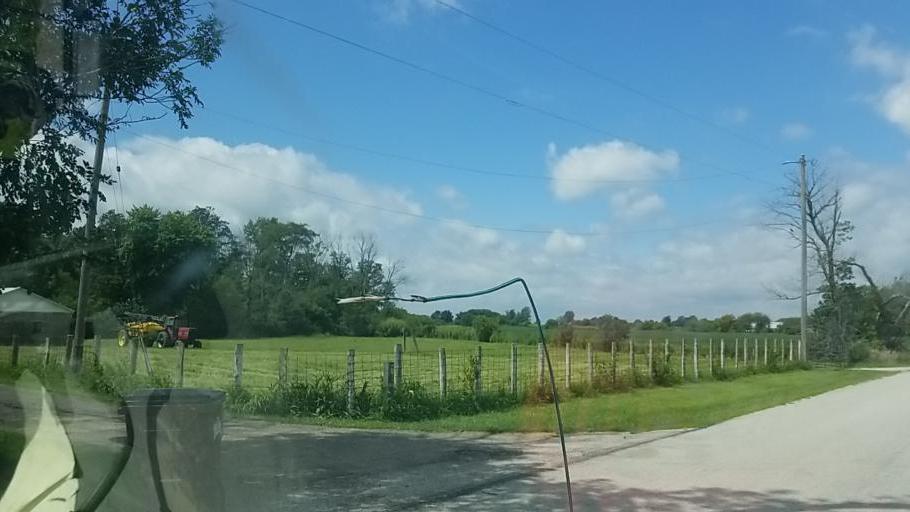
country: US
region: Ohio
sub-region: Clark County
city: South Charleston
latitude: 39.7472
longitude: -83.6720
